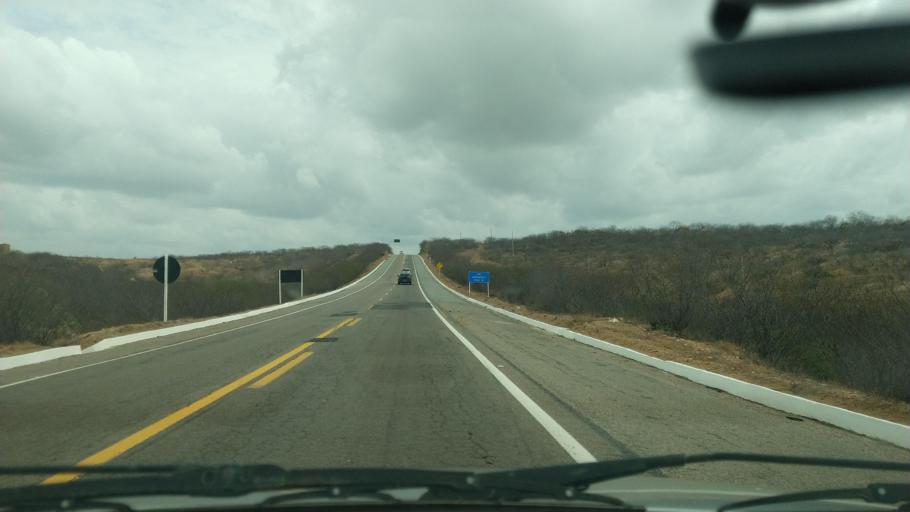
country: BR
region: Rio Grande do Norte
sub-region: Currais Novos
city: Currais Novos
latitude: -6.2193
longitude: -36.4262
